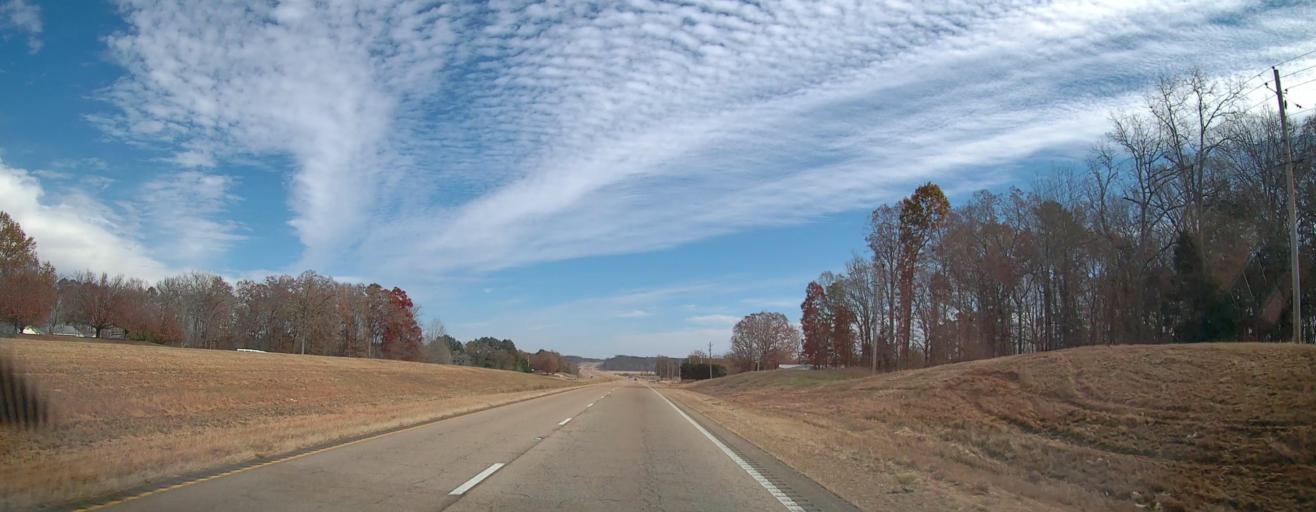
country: US
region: Mississippi
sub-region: Alcorn County
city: Corinth
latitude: 34.9310
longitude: -88.6817
